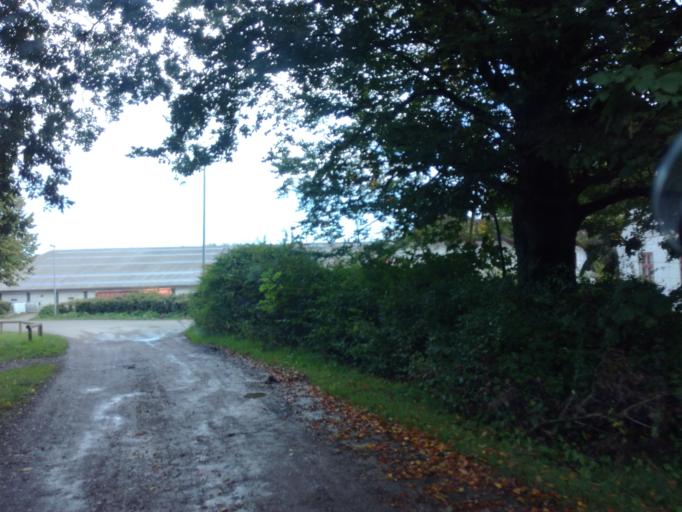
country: DK
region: South Denmark
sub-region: Fredericia Kommune
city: Snoghoj
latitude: 55.5607
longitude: 9.7021
